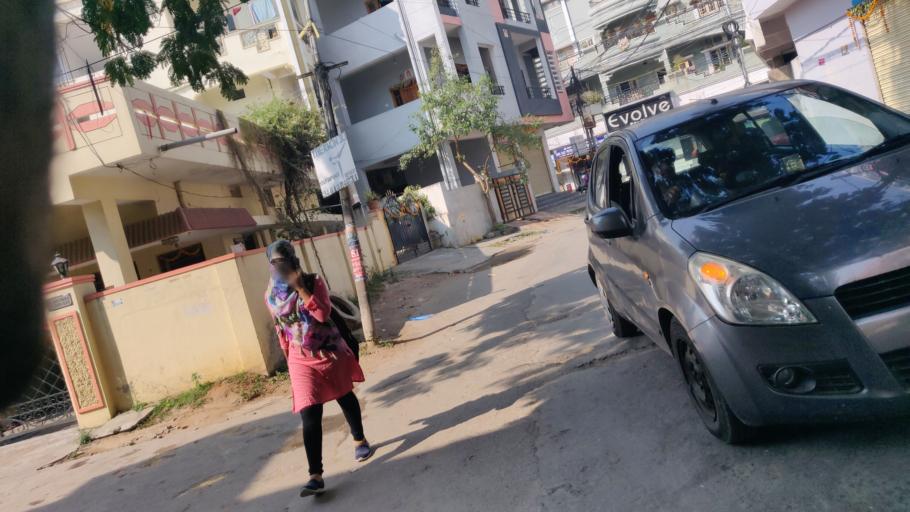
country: IN
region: Telangana
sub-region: Rangareddi
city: Gaddi Annaram
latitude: 17.3646
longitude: 78.5270
